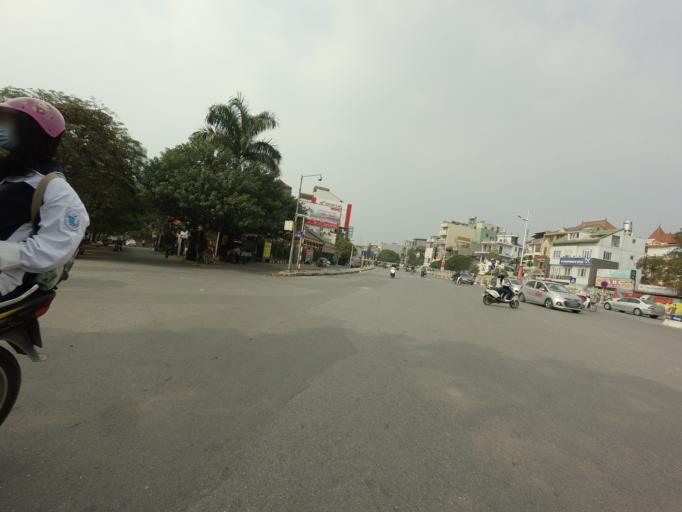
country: VN
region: Ha Noi
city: Tay Ho
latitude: 21.0588
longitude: 105.8337
